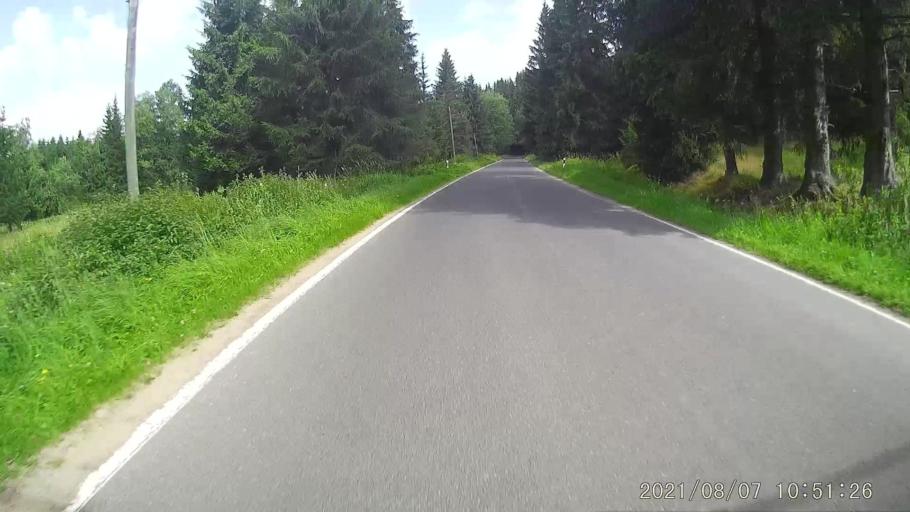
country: PL
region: Lower Silesian Voivodeship
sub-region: Powiat klodzki
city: Polanica-Zdroj
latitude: 50.2892
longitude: 16.4684
